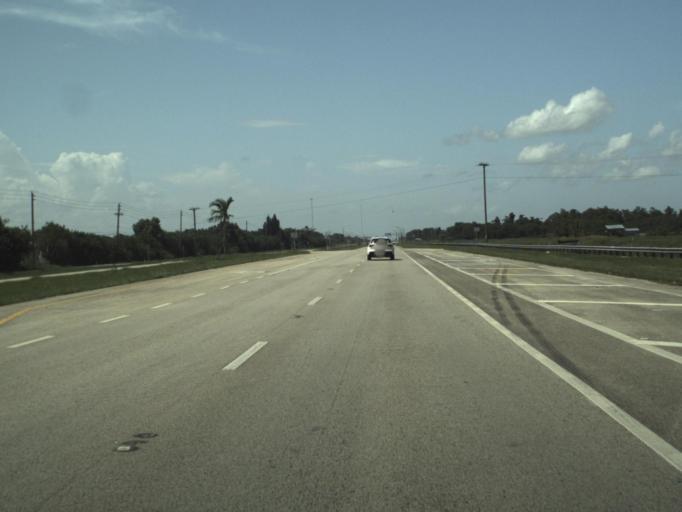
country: US
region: Florida
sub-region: Palm Beach County
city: Villages of Oriole
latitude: 26.5185
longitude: -80.2052
